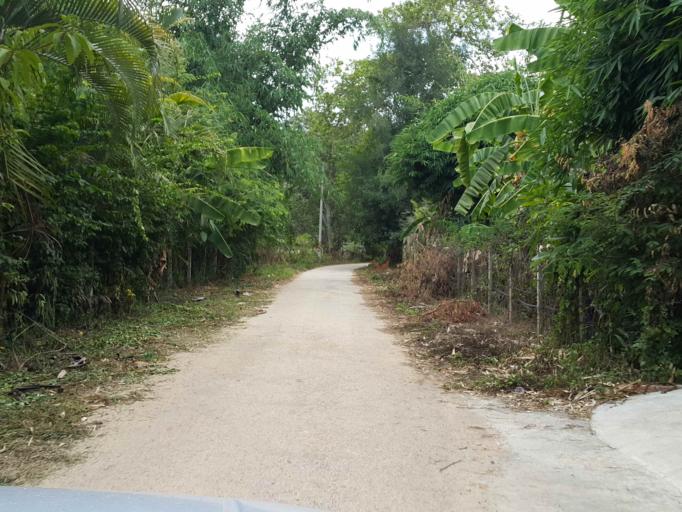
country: TH
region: Chiang Mai
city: Hang Dong
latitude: 18.7564
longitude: 98.9025
